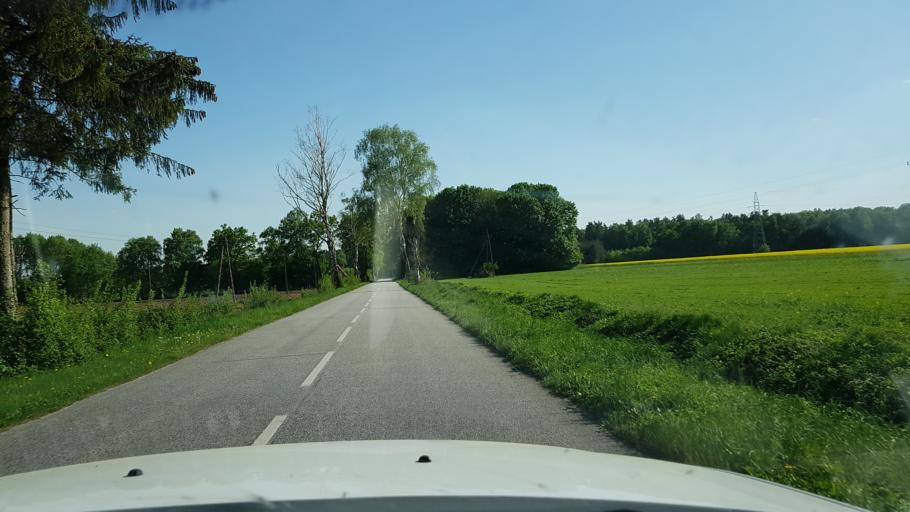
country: PL
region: West Pomeranian Voivodeship
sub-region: Powiat lobeski
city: Resko
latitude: 53.8219
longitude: 15.3955
